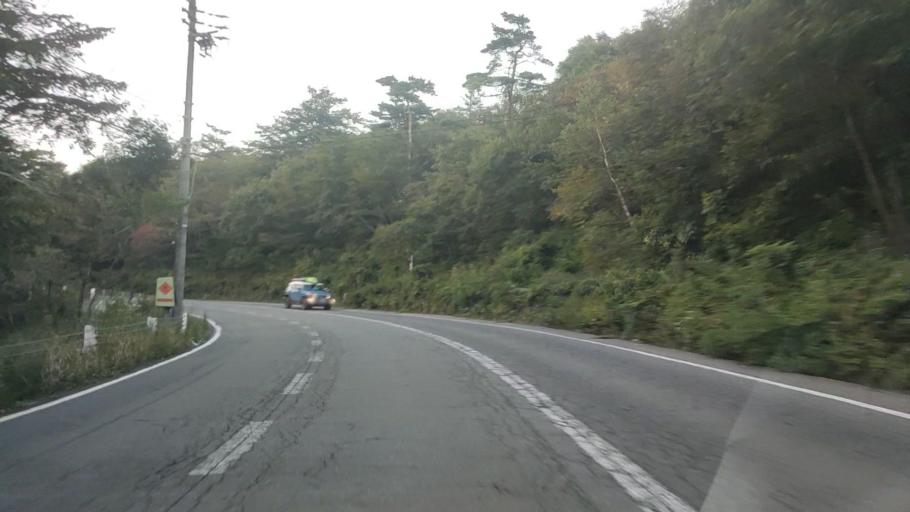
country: JP
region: Nagano
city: Komoro
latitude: 36.3958
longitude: 138.5798
